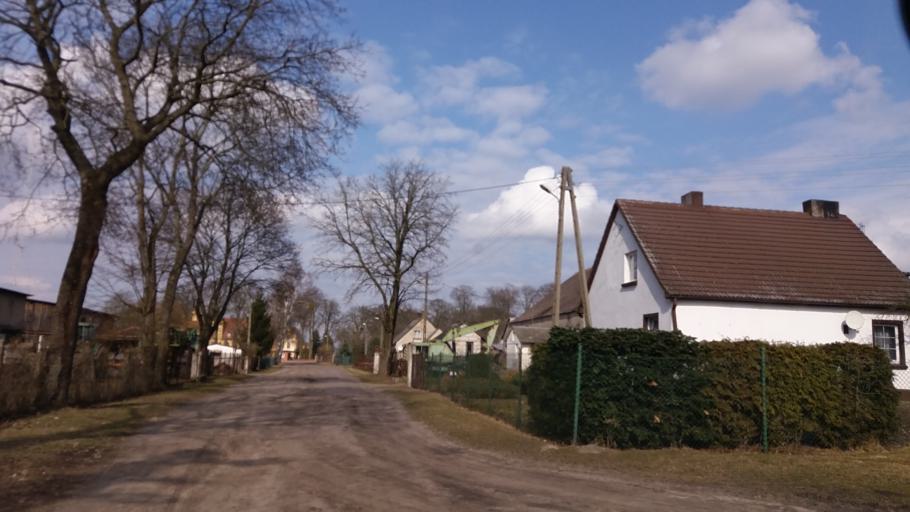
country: PL
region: West Pomeranian Voivodeship
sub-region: Powiat choszczenski
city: Drawno
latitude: 53.1440
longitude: 15.6816
